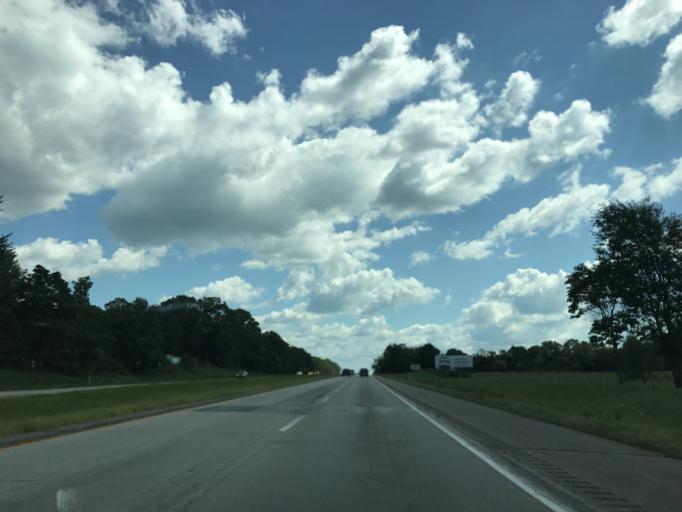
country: US
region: Indiana
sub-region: Marshall County
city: Plymouth
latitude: 41.3645
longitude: -86.4002
